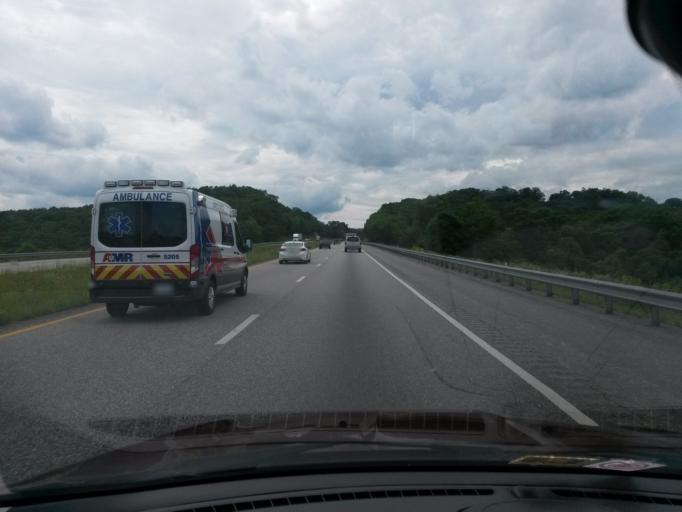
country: US
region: Virginia
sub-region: Alleghany County
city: Clifton Forge
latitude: 37.8300
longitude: -79.8116
